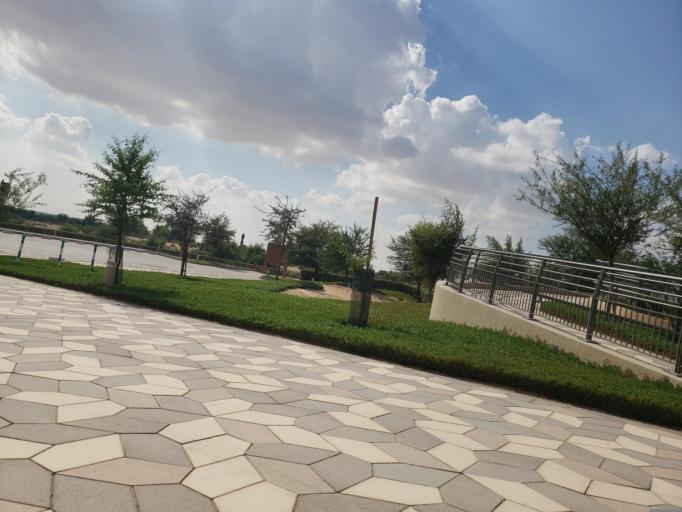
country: AE
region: Dubai
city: Dubai
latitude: 24.8457
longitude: 55.2489
